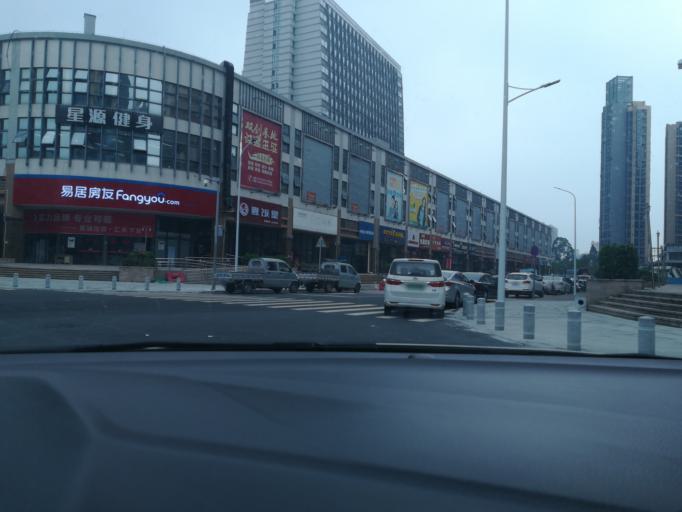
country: CN
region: Guangdong
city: Nansha
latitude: 22.8013
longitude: 113.5339
